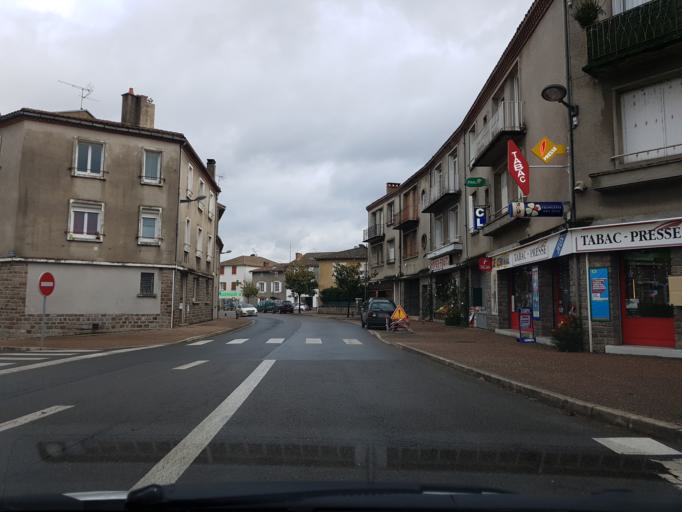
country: FR
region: Poitou-Charentes
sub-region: Departement de la Charente
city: Chabanais
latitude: 45.8735
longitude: 0.7183
